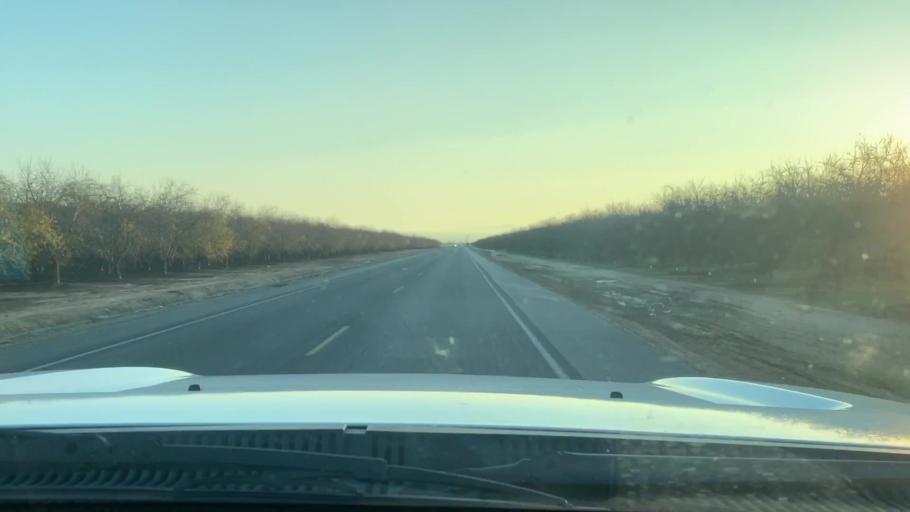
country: US
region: California
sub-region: Kern County
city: Wasco
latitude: 35.5003
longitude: -119.3973
